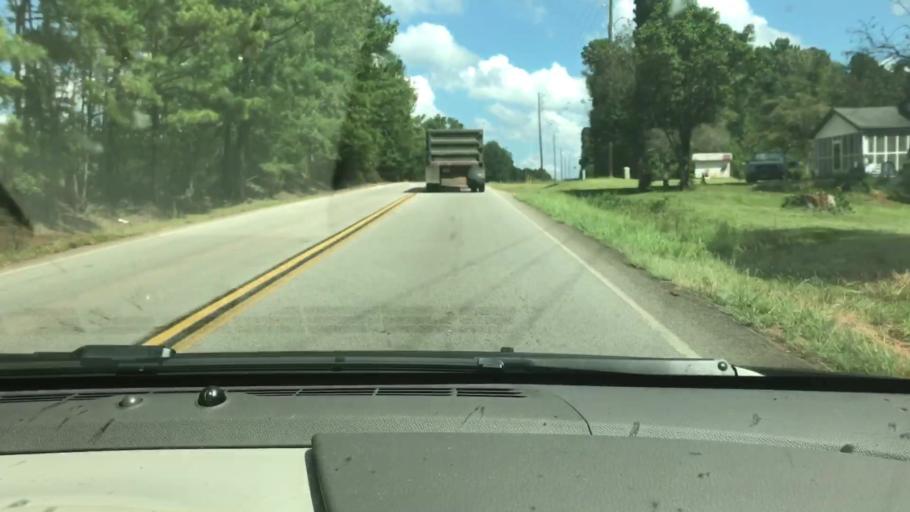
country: US
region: Alabama
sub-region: Chambers County
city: Valley
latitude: 32.8439
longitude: -85.0351
